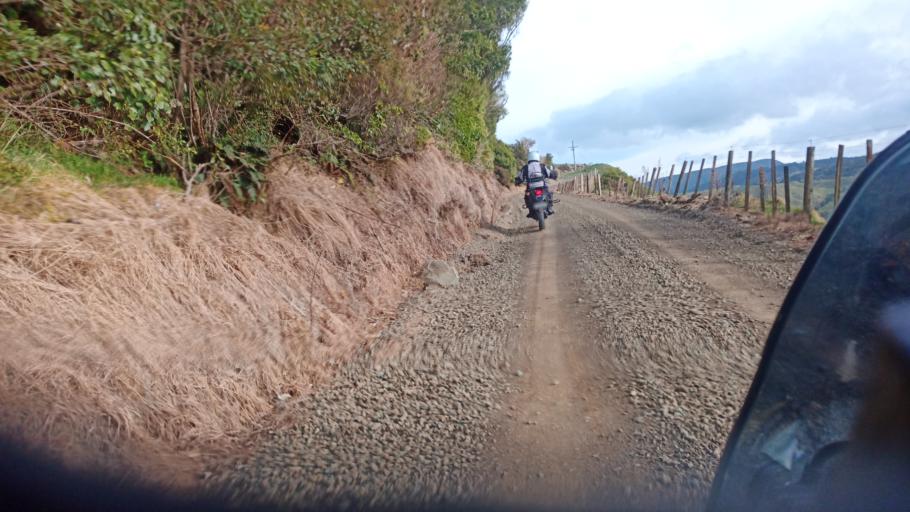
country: NZ
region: Gisborne
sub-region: Gisborne District
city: Gisborne
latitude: -38.4643
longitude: 177.5353
